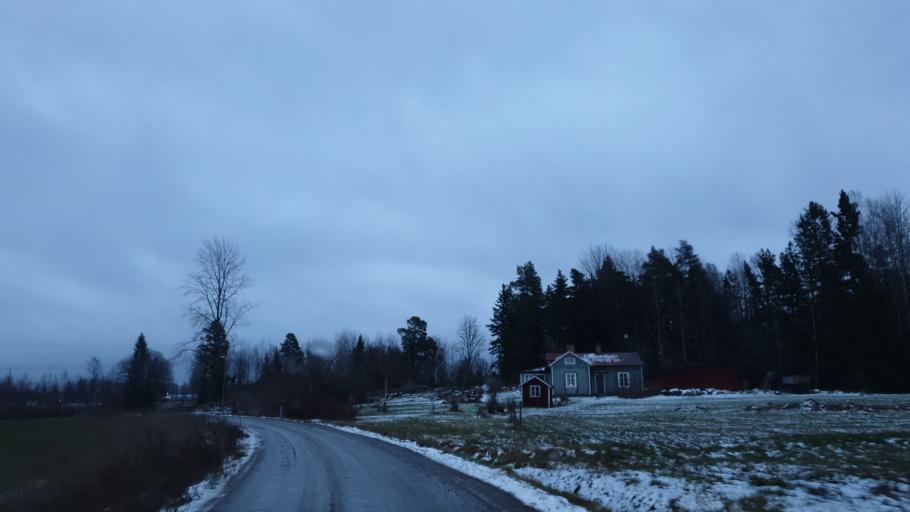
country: SE
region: Uppsala
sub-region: Tierps Kommun
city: Tierp
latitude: 60.3393
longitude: 17.4768
